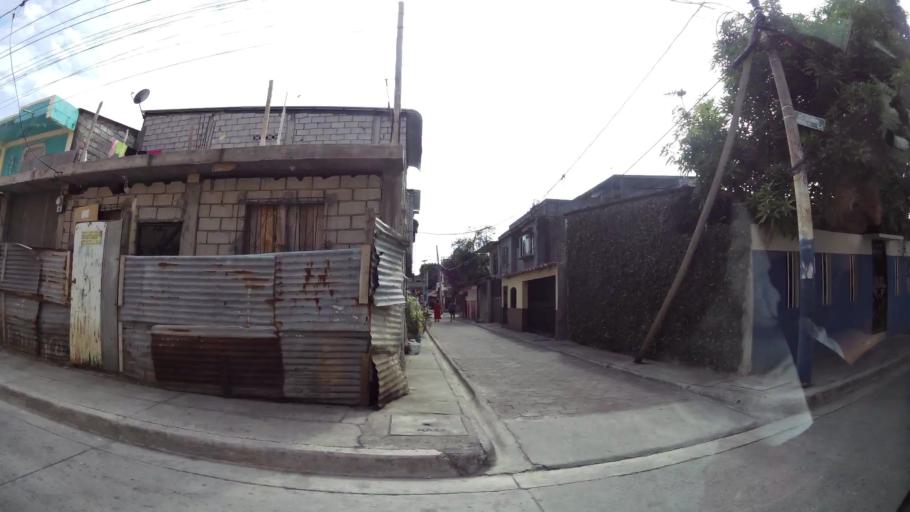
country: EC
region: Guayas
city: Guayaquil
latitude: -2.2535
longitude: -79.8772
